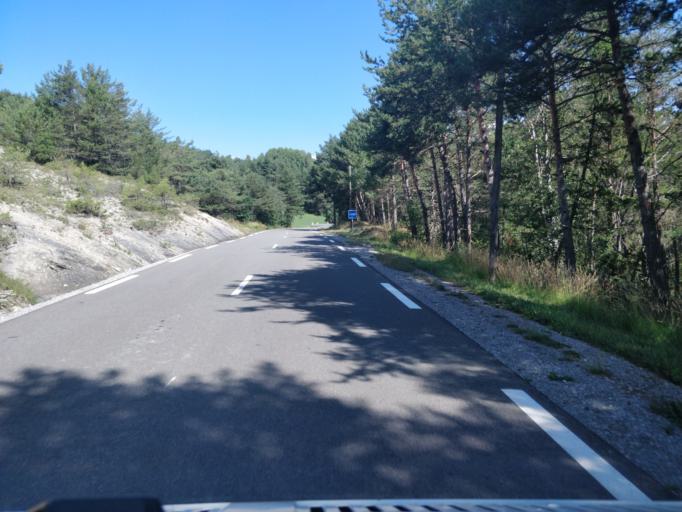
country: FR
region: Provence-Alpes-Cote d'Azur
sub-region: Departement des Alpes-de-Haute-Provence
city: Seyne-les-Alpes
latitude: 44.4120
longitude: 6.3376
